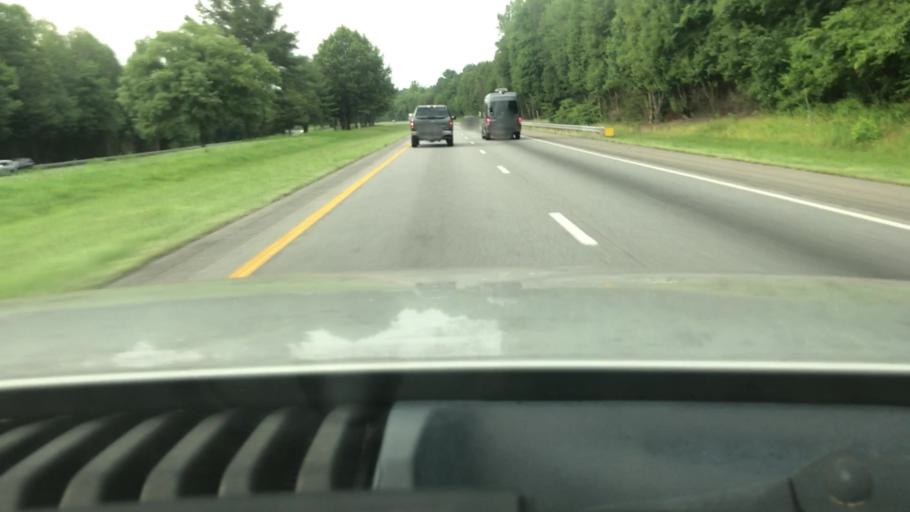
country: US
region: North Carolina
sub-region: Surry County
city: Dobson
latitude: 36.3429
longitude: -80.7944
